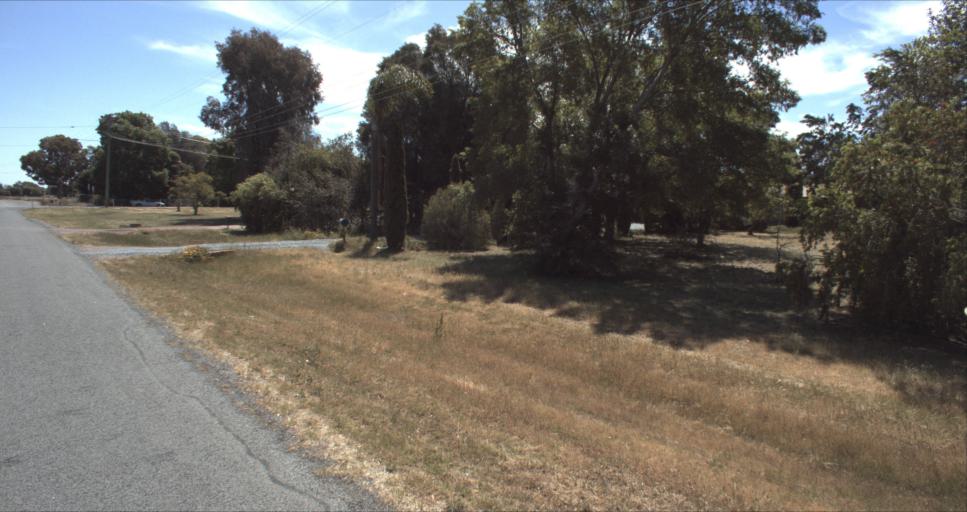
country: AU
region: New South Wales
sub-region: Leeton
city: Leeton
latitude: -34.5718
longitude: 146.4143
